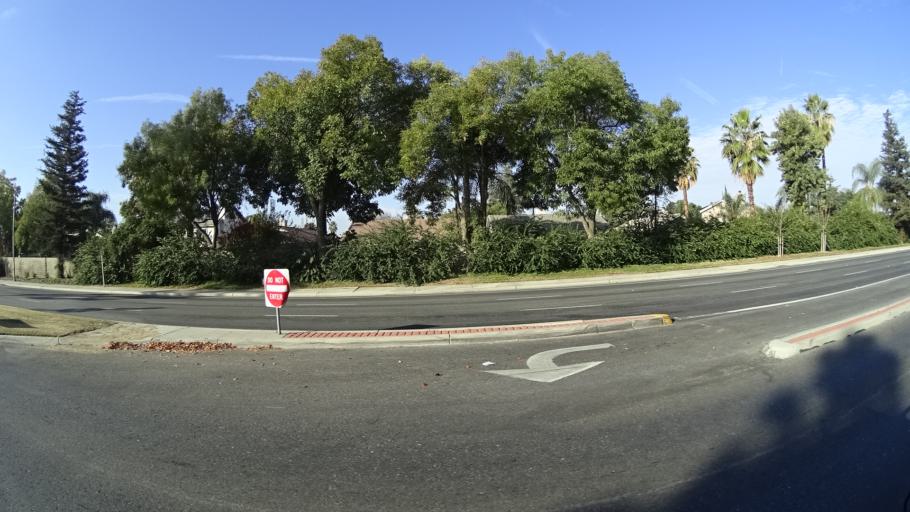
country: US
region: California
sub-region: Kern County
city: Greenacres
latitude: 35.3210
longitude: -119.0921
